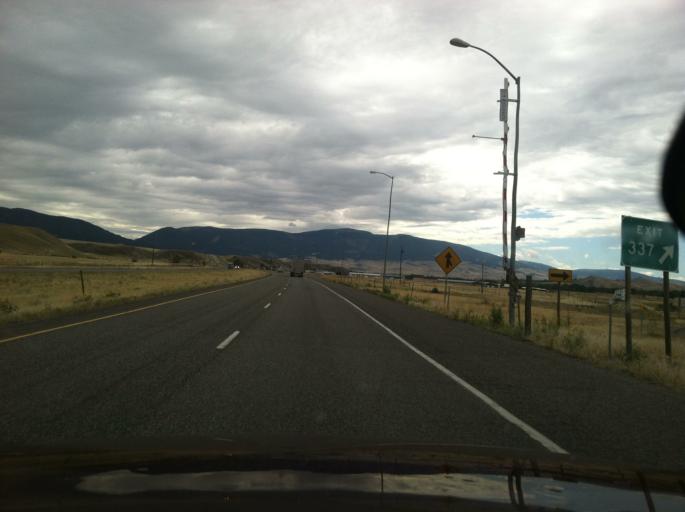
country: US
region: Montana
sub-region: Park County
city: Livingston
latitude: 45.6863
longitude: -110.5033
